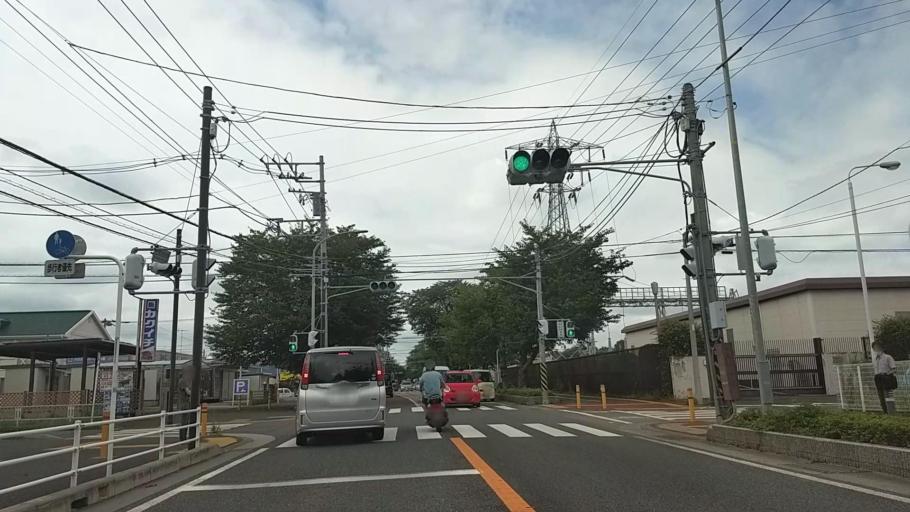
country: JP
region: Kanagawa
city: Minami-rinkan
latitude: 35.4354
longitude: 139.4669
